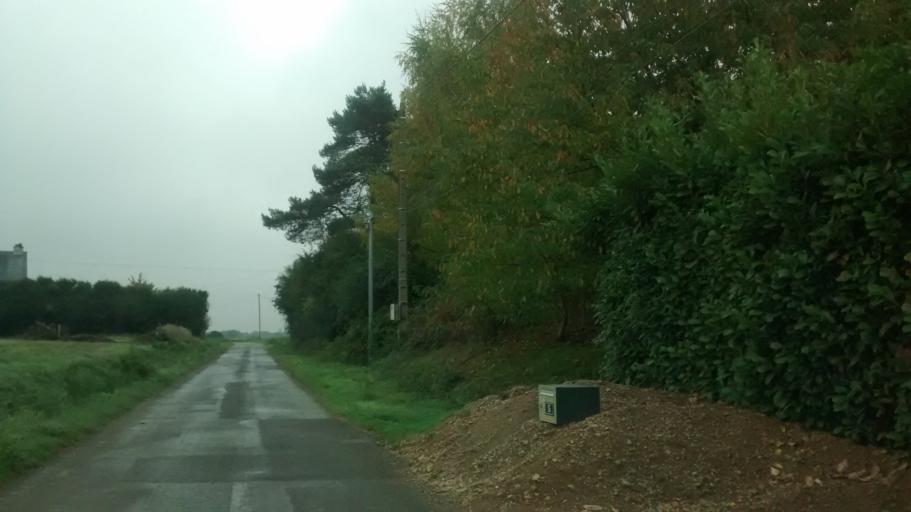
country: FR
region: Brittany
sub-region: Departement d'Ille-et-Vilaine
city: Breteil
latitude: 48.1177
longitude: -1.8985
